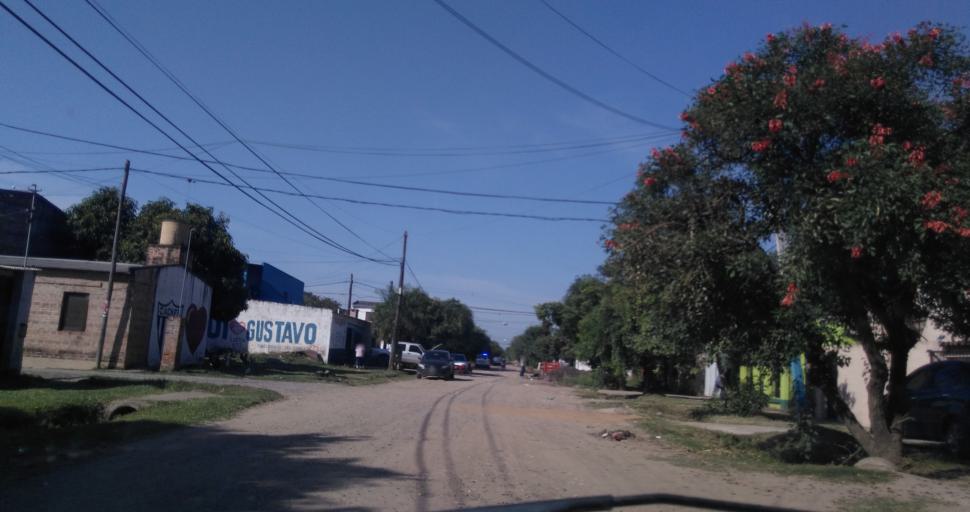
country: AR
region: Chaco
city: Resistencia
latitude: -27.4682
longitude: -58.9713
